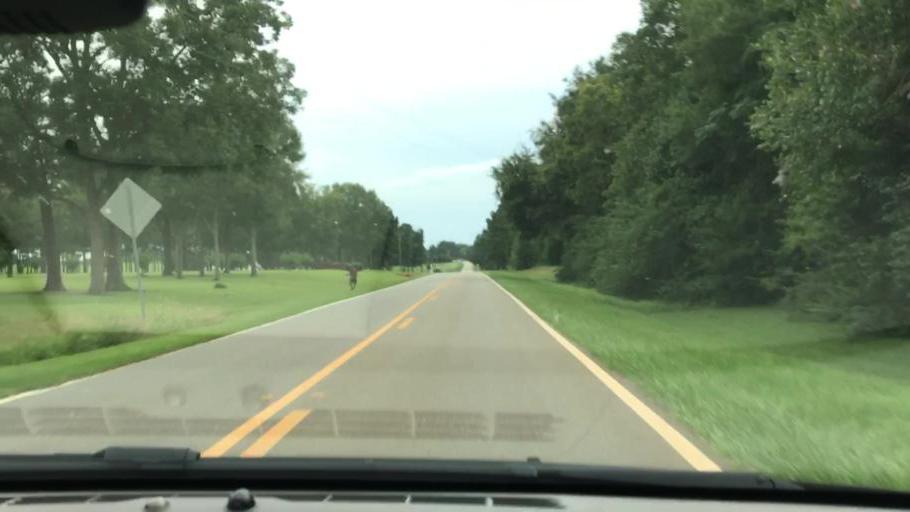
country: US
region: Georgia
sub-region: Early County
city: Blakely
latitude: 31.4419
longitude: -84.9147
